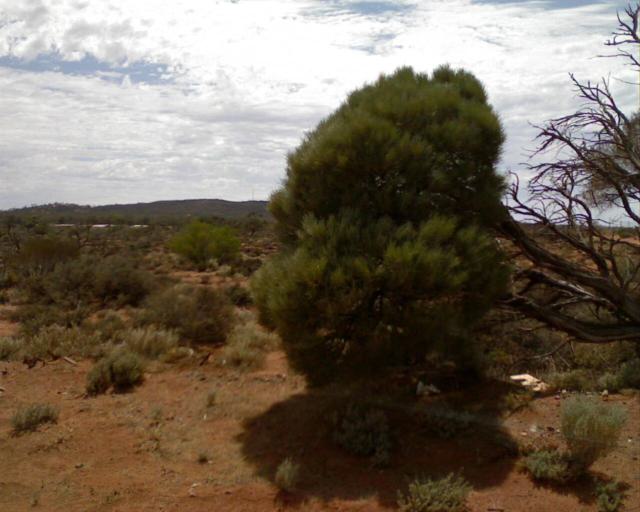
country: AU
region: Western Australia
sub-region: Kalgoorlie/Boulder
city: Stoneville
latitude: -31.2166
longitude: 121.6495
